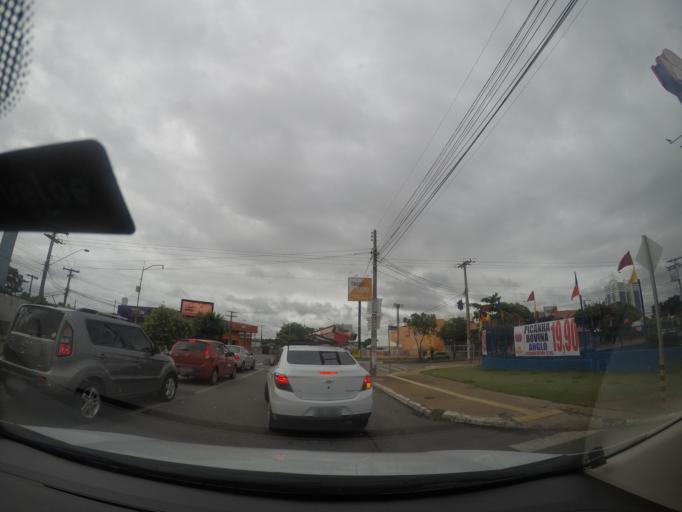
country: BR
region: Goias
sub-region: Goiania
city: Goiania
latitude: -16.7449
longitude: -49.2819
